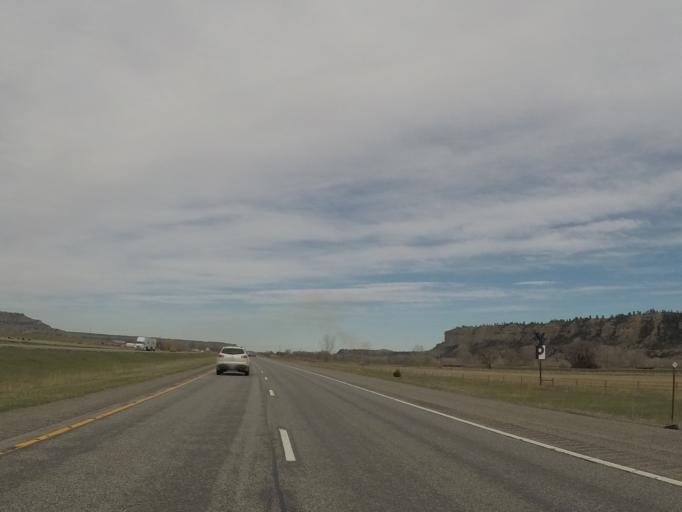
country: US
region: Montana
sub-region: Stillwater County
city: Columbus
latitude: 45.6037
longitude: -109.0371
